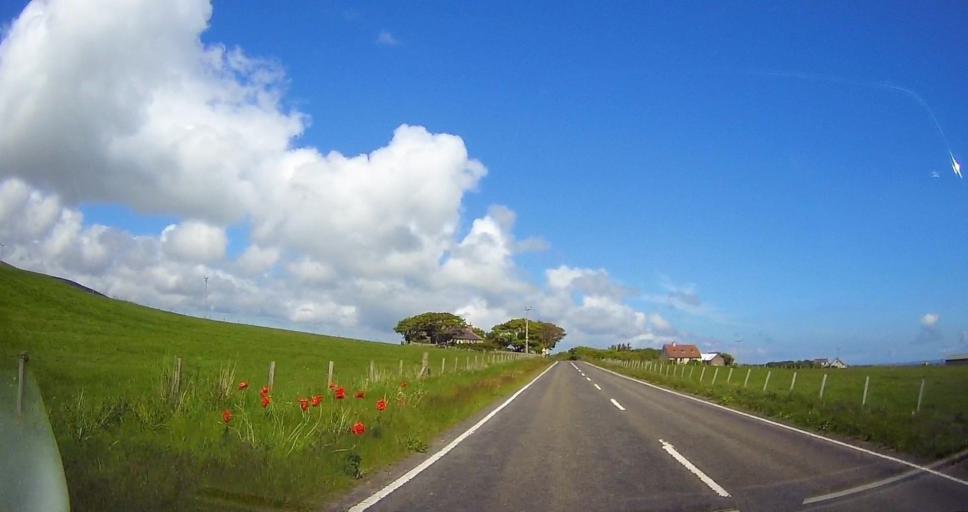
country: GB
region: Scotland
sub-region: Orkney Islands
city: Orkney
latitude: 59.0209
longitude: -3.0996
